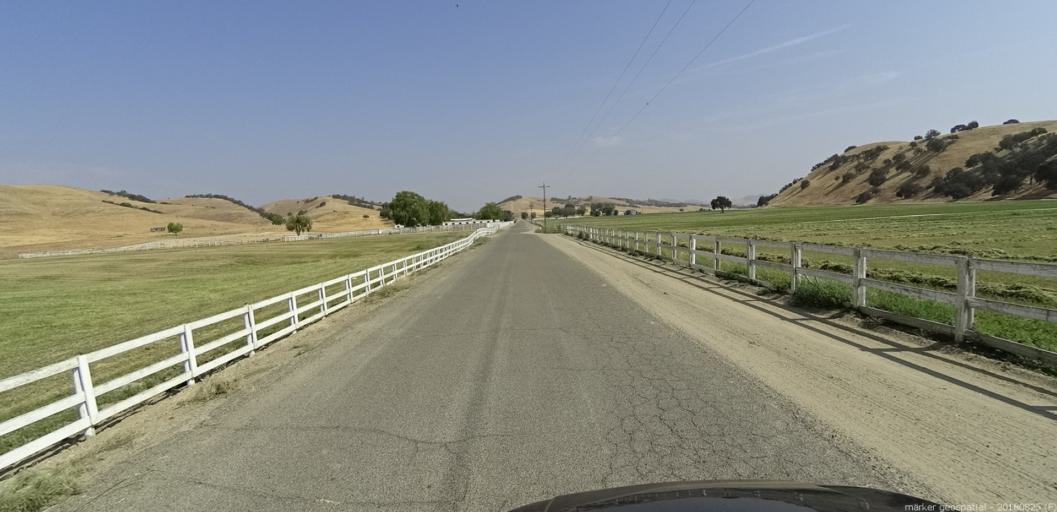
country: US
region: California
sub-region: San Luis Obispo County
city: San Miguel
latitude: 35.8270
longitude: -120.6563
